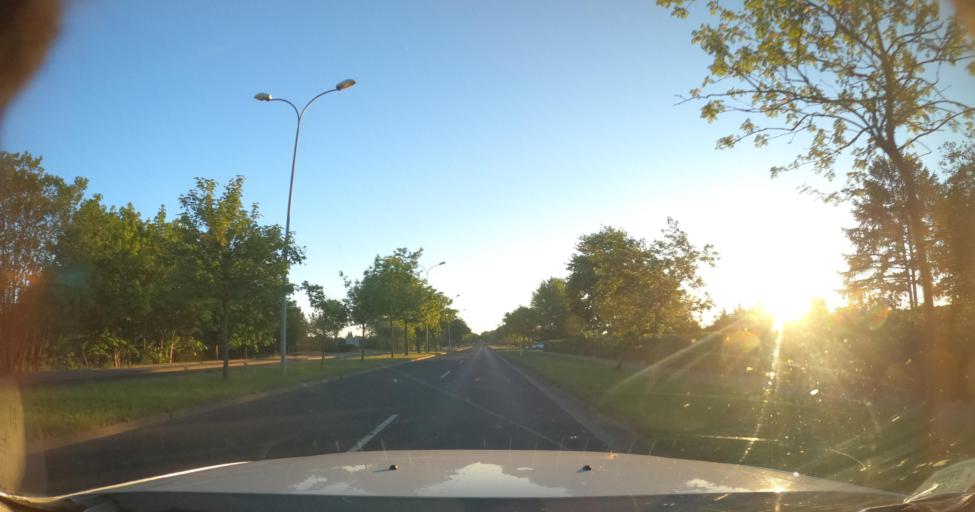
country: PL
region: Pomeranian Voivodeship
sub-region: Slupsk
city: Slupsk
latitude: 54.4701
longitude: 17.0741
